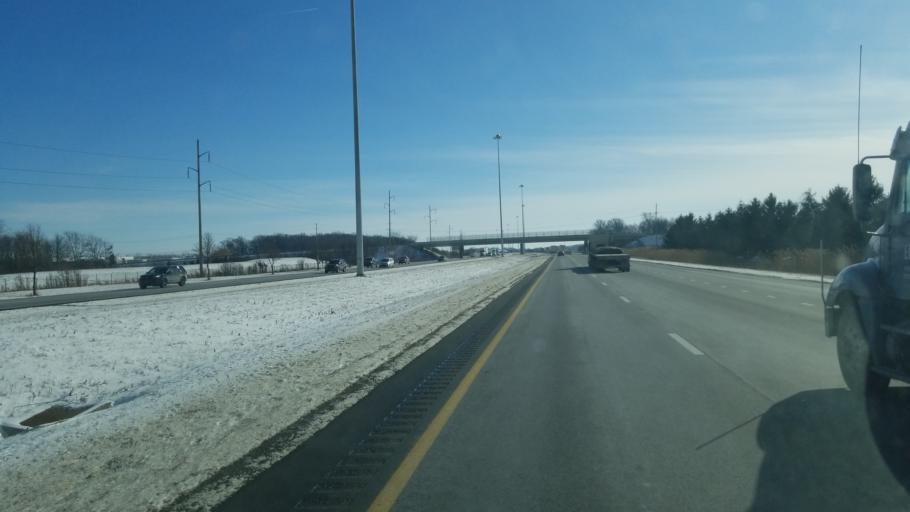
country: US
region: Ohio
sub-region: Lucas County
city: Maumee
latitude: 41.5742
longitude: -83.6914
